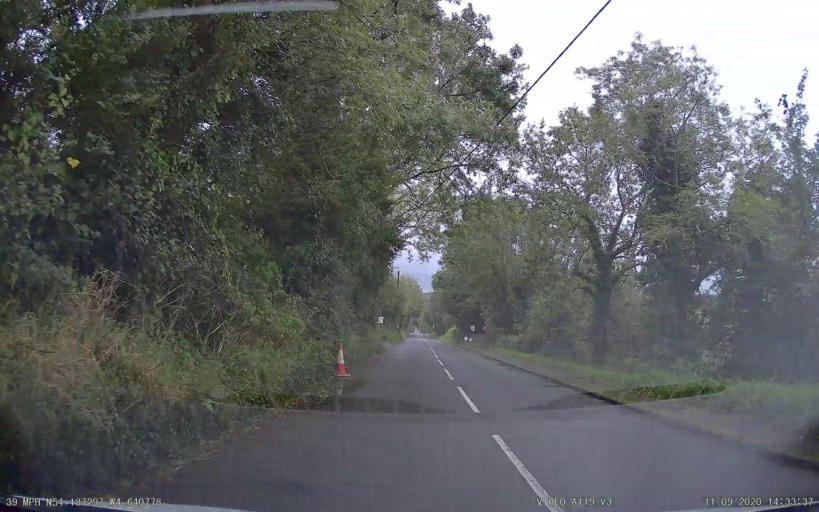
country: IM
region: Castletown
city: Castletown
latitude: 54.1873
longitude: -4.6408
